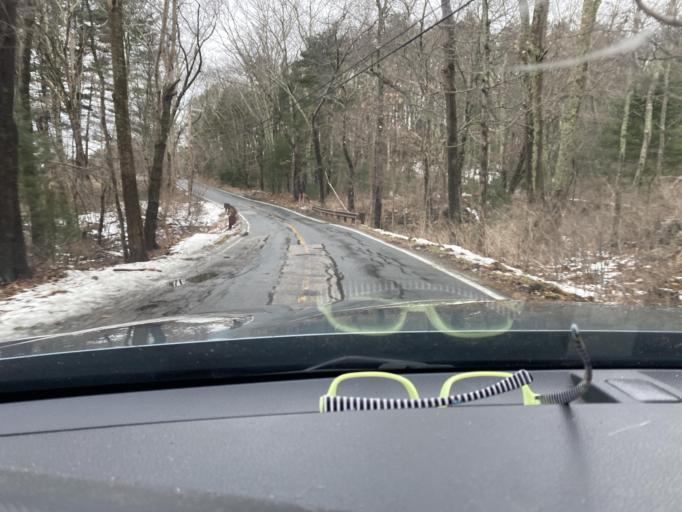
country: US
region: Massachusetts
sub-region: Middlesex County
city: Sherborn
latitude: 42.2118
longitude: -71.3840
